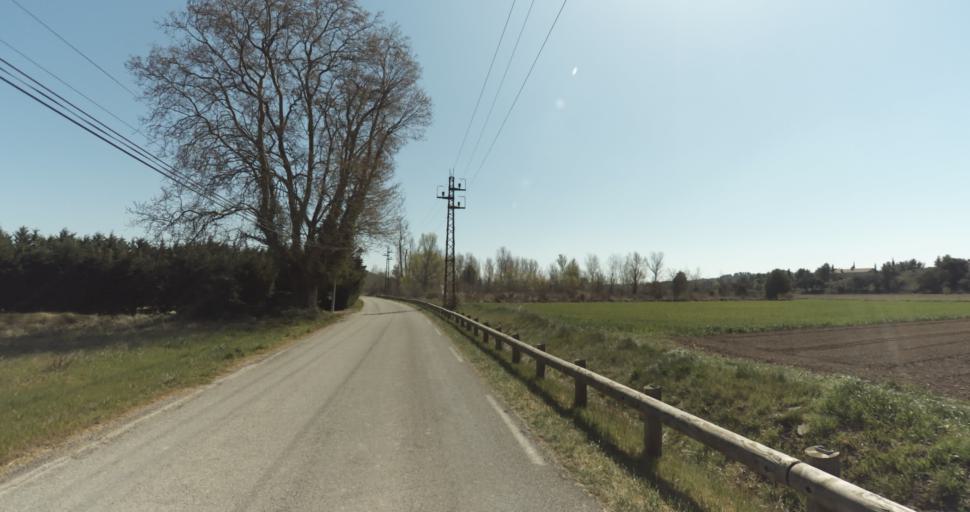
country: FR
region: Provence-Alpes-Cote d'Azur
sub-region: Departement des Bouches-du-Rhone
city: Pelissanne
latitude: 43.6176
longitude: 5.1631
